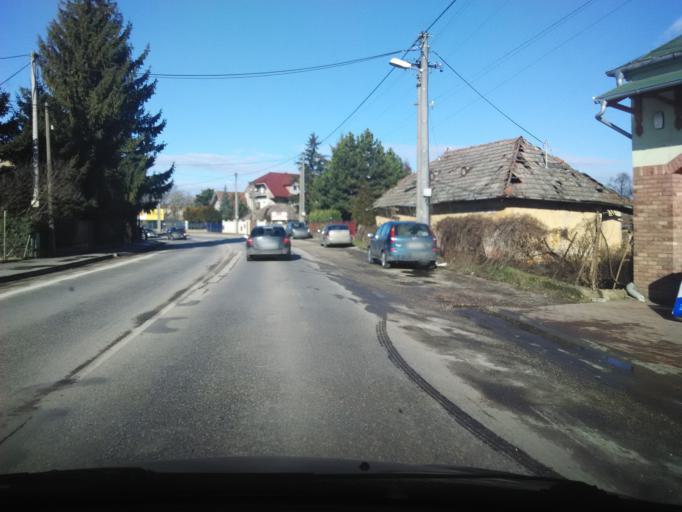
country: SK
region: Nitriansky
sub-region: Okres Nitra
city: Nitra
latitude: 48.2373
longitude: 18.1226
